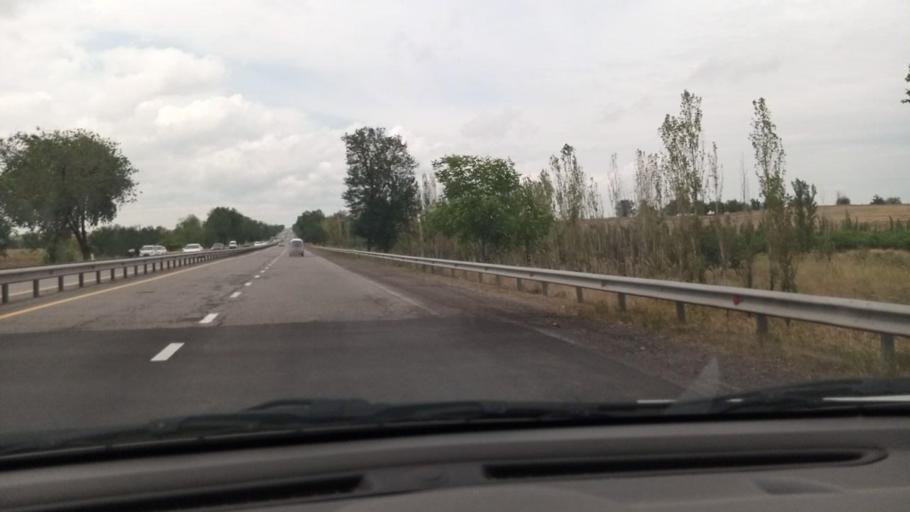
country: UZ
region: Toshkent
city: Ohangaron
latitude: 40.9982
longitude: 69.5282
